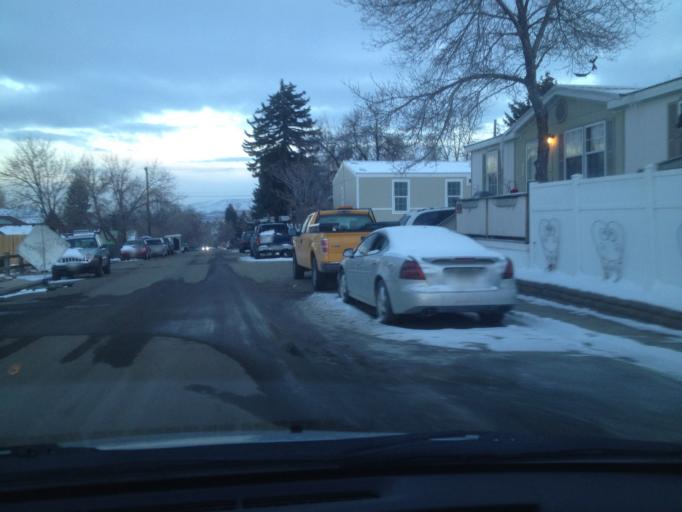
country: US
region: Colorado
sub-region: Jefferson County
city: Golden
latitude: 39.7633
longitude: -105.2305
